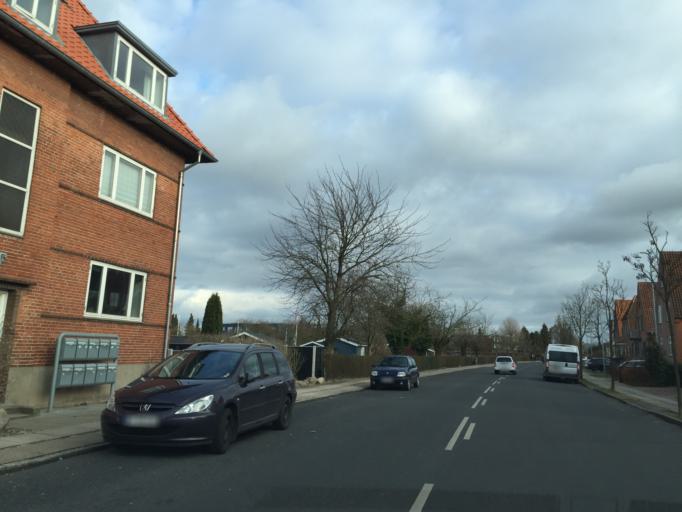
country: DK
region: South Denmark
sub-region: Odense Kommune
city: Odense
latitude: 55.3909
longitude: 10.4022
